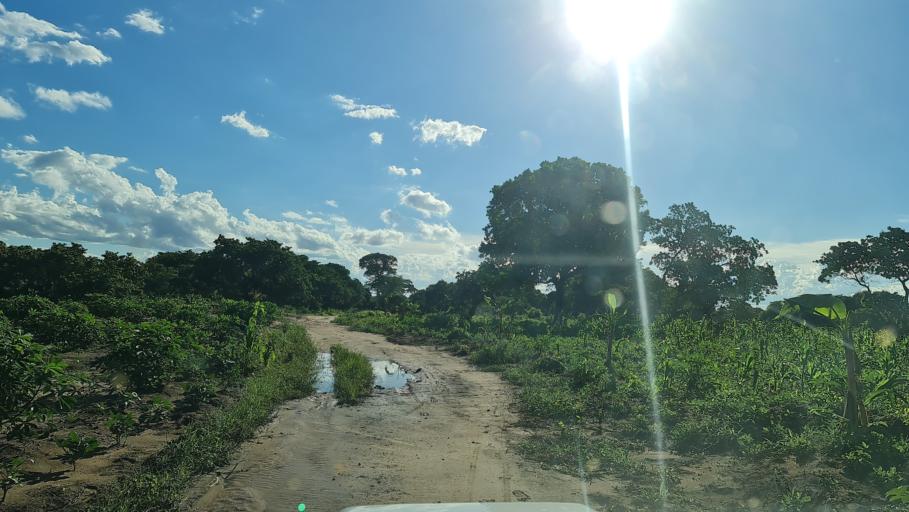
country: MZ
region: Nampula
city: Ilha de Mocambique
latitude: -14.9303
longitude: 40.2194
